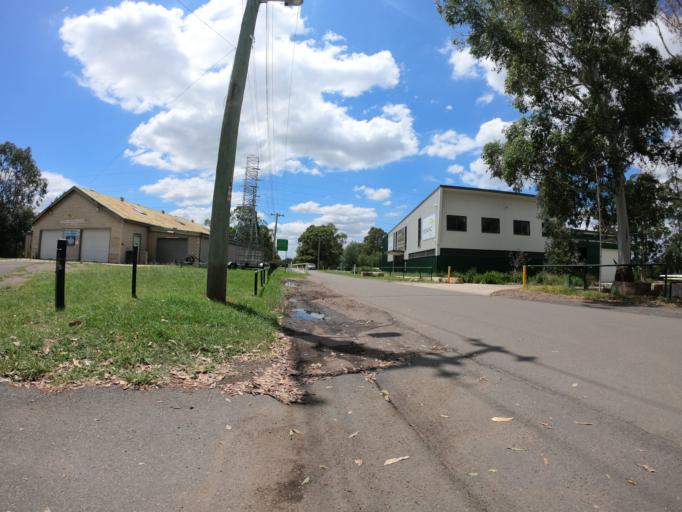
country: AU
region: New South Wales
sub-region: Penrith Municipality
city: Penrith
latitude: -33.7455
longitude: 150.6842
